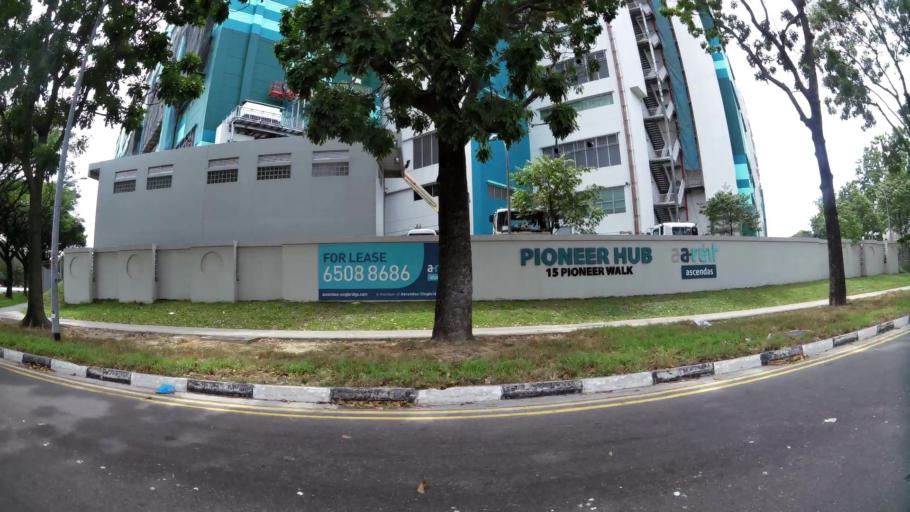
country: MY
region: Johor
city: Johor Bahru
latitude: 1.3223
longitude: 103.6963
